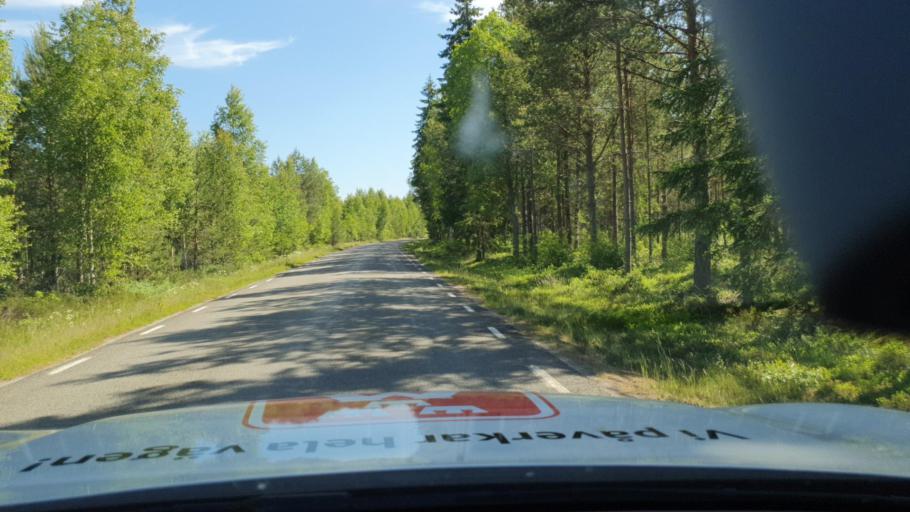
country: SE
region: Vaestra Goetaland
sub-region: Tidaholms Kommun
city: Olofstorp
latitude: 58.2805
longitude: 13.9914
